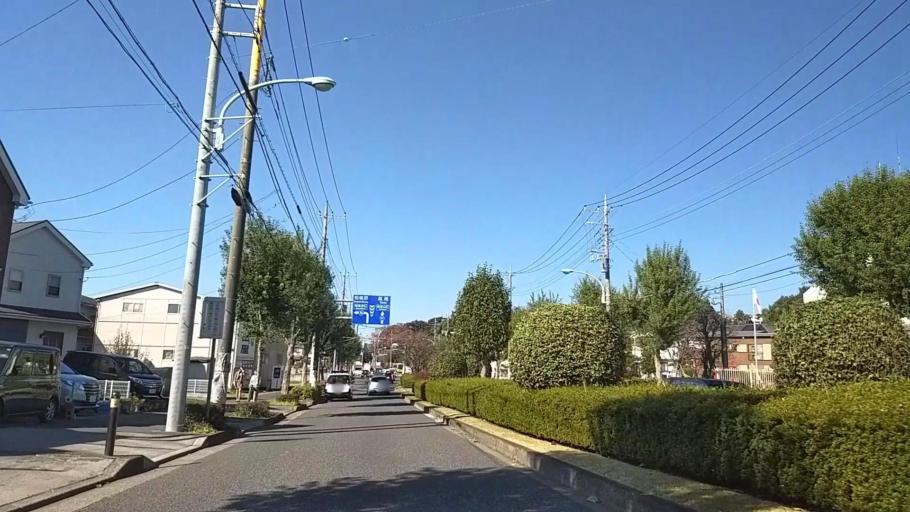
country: JP
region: Tokyo
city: Hachioji
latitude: 35.6045
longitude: 139.3441
